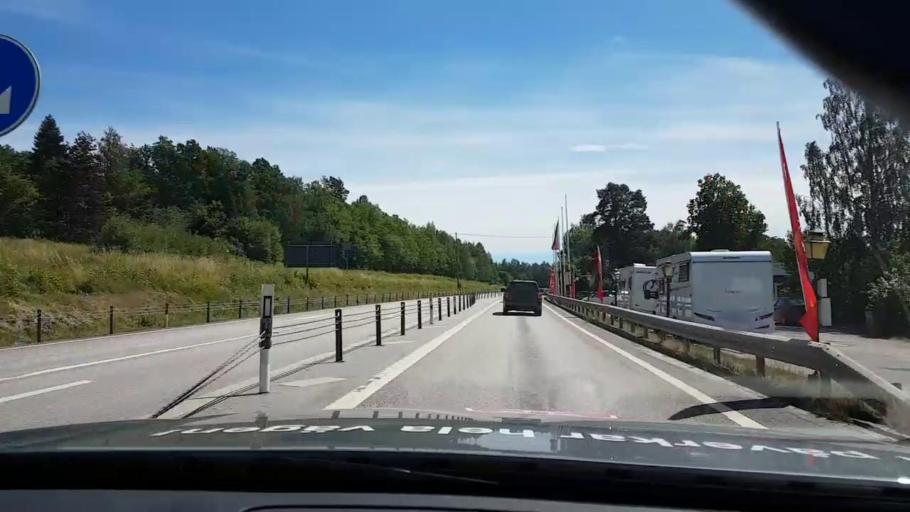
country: SE
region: Kalmar
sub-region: Vasterviks Kommun
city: Vaestervik
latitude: 57.7981
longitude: 16.5157
